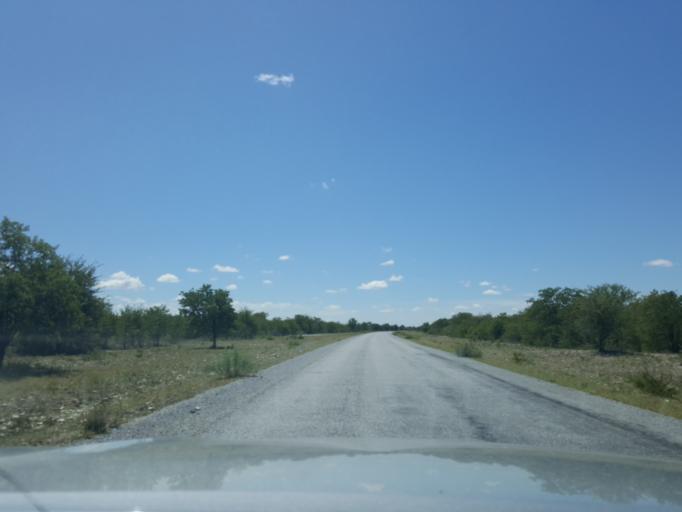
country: BW
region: Central
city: Gweta
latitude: -20.1686
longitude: 25.3960
